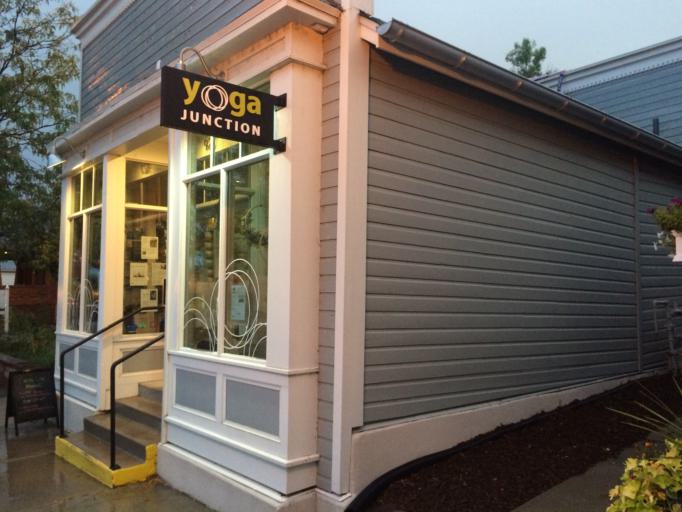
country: US
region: Colorado
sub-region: Boulder County
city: Louisville
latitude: 39.9794
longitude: -105.1322
